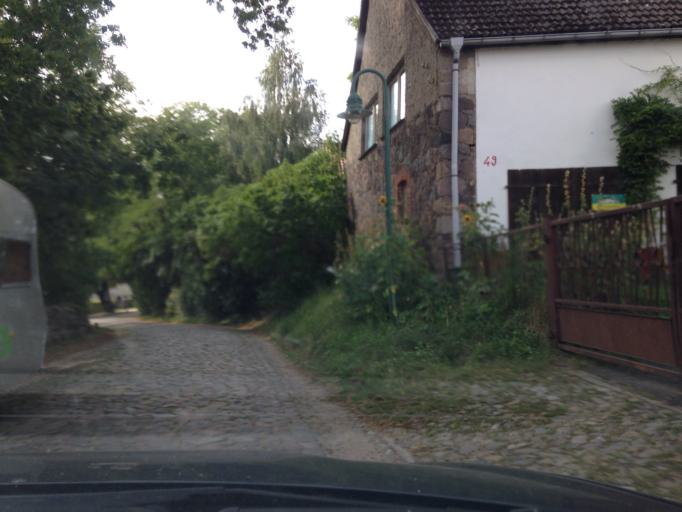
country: DE
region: Mecklenburg-Vorpommern
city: Loitz
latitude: 53.3023
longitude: 13.4399
